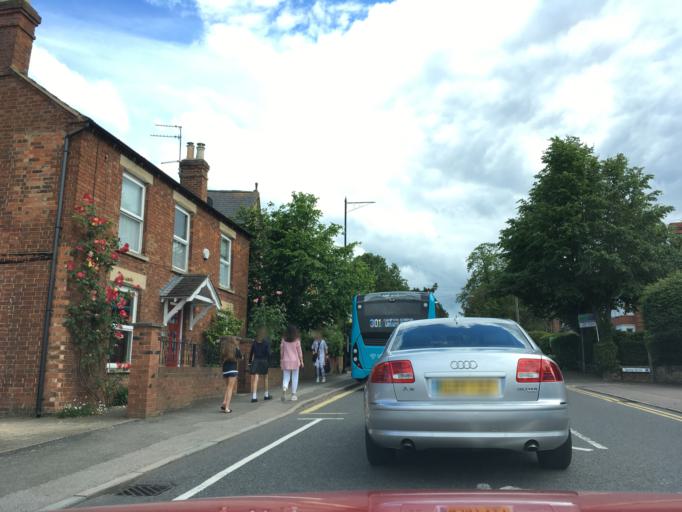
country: GB
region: England
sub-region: Milton Keynes
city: Woburn Sands
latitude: 52.0155
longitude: -0.6495
